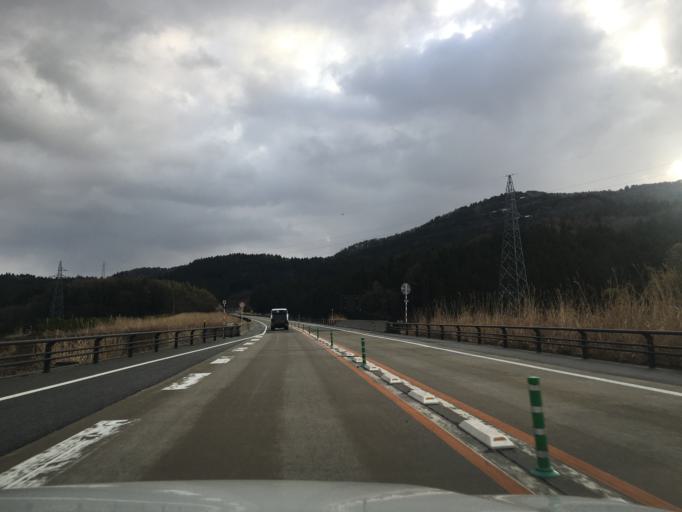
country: JP
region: Yamagata
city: Tsuruoka
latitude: 38.6901
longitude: 139.6755
